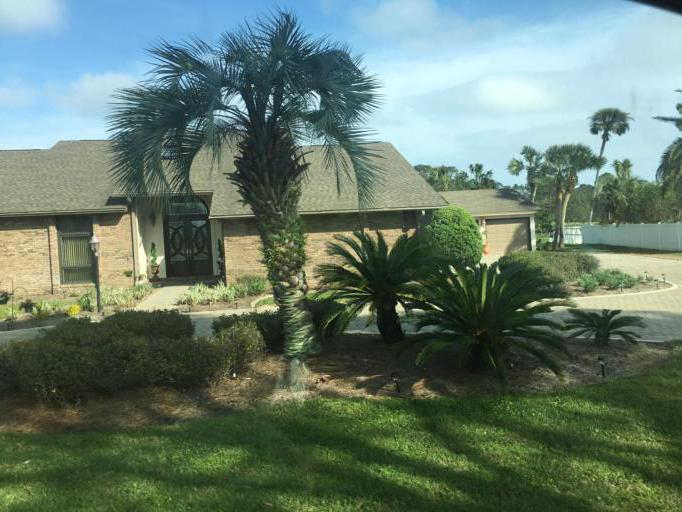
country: US
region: Florida
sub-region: Bay County
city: Panama City Beach
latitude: 30.2173
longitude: -85.8402
